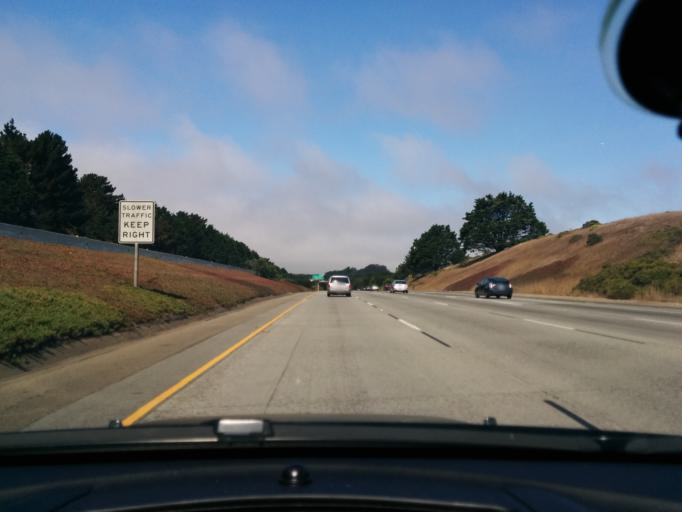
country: US
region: California
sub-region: San Mateo County
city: Colma
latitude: 37.6546
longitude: -122.4569
